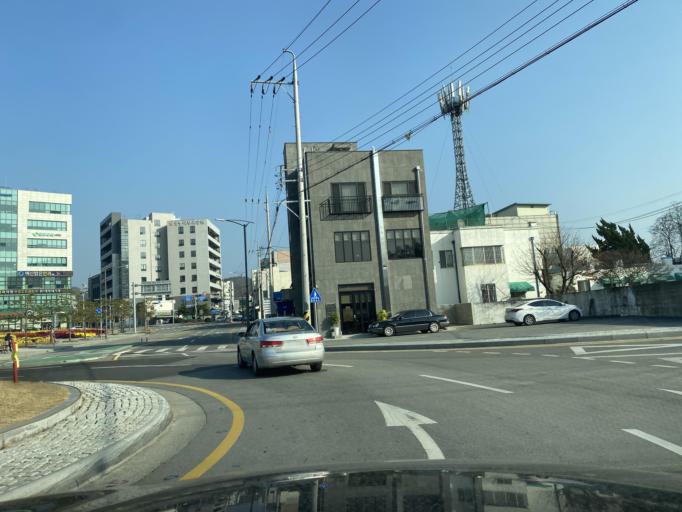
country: KR
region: Chungcheongnam-do
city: Yesan
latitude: 36.6784
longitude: 126.8433
